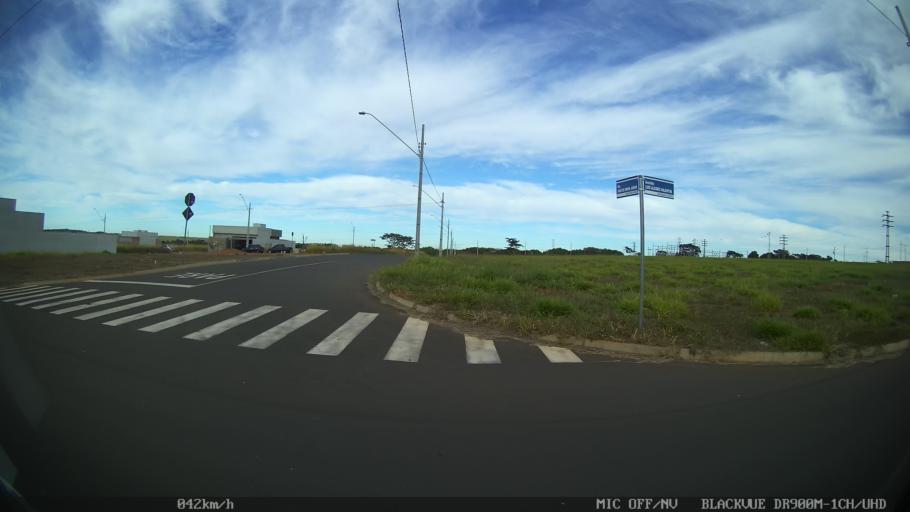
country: BR
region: Sao Paulo
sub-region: Catanduva
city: Catanduva
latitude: -21.1366
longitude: -49.0131
